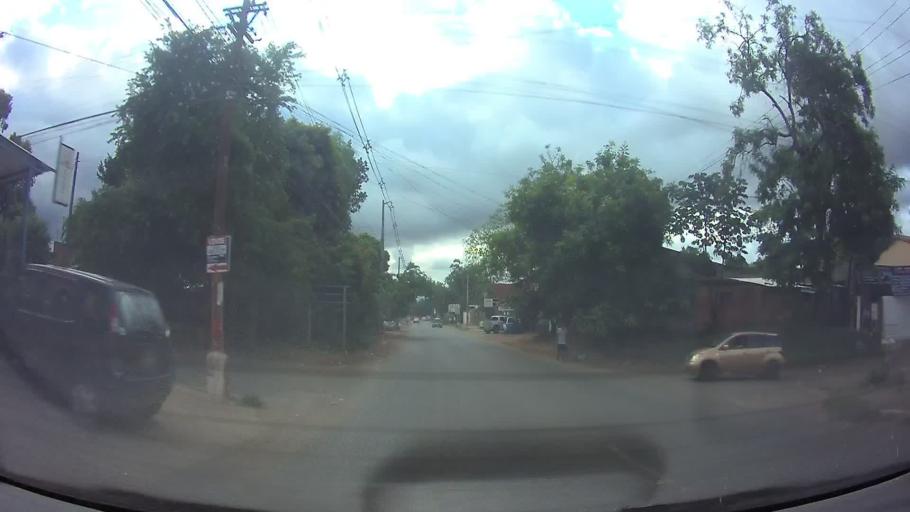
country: PY
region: Central
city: Fernando de la Mora
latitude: -25.3182
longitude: -57.5409
